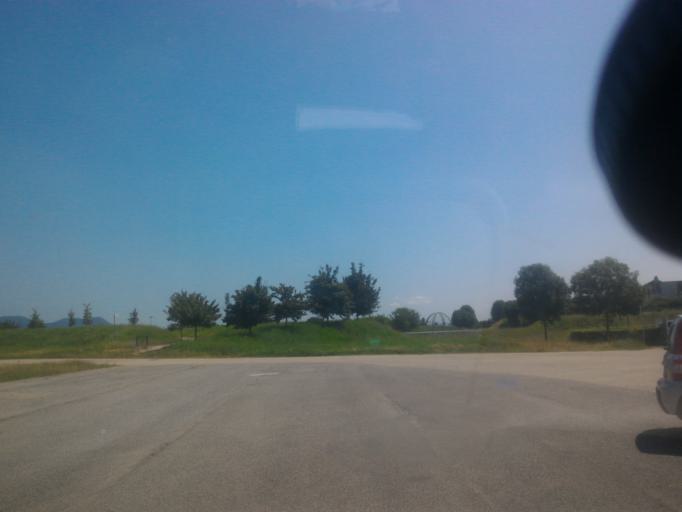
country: IT
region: Piedmont
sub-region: Provincia di Torino
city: Pinerolo
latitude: 44.8902
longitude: 7.3505
